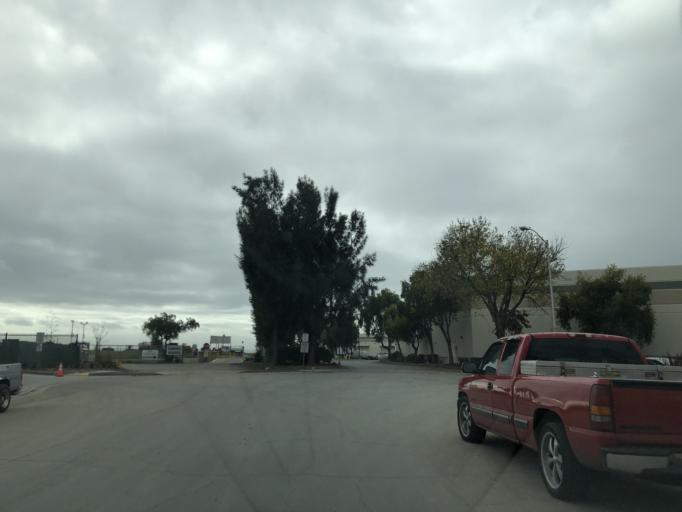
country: US
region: California
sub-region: Alameda County
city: Newark
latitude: 37.5191
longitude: -122.0337
